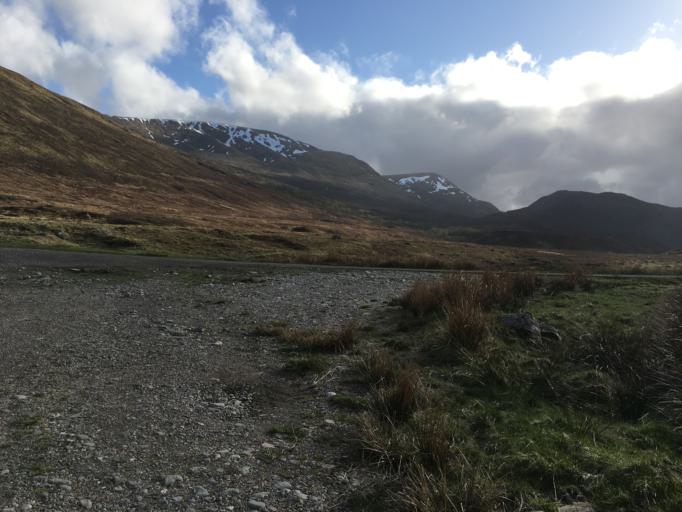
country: GB
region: Scotland
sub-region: Highland
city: Kingussie
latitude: 57.0207
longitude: -4.4377
